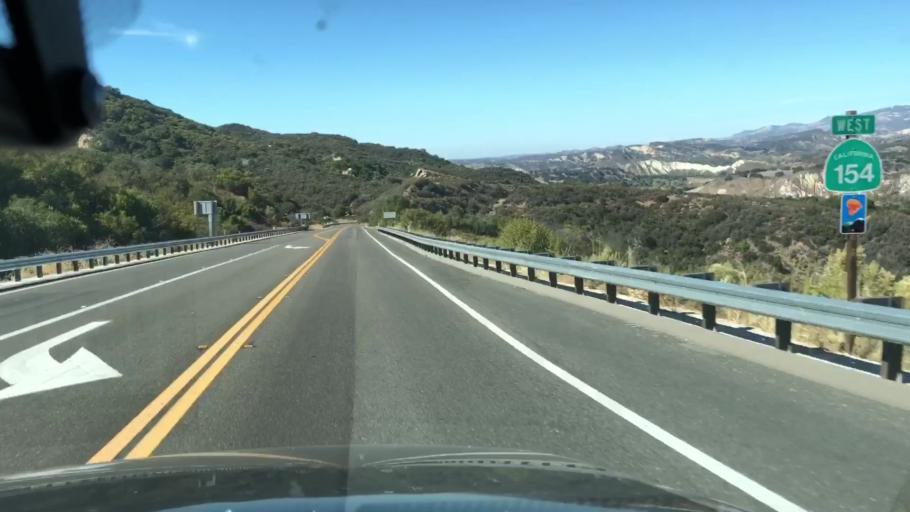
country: US
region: California
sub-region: Santa Barbara County
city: Goleta
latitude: 34.5339
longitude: -119.8583
